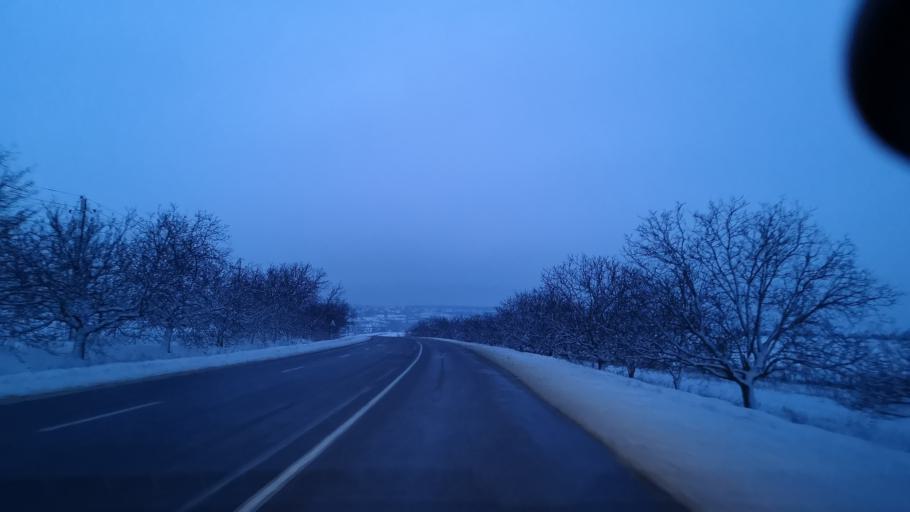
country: MD
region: Soldanesti
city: Soldanesti
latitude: 47.7168
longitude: 28.8477
